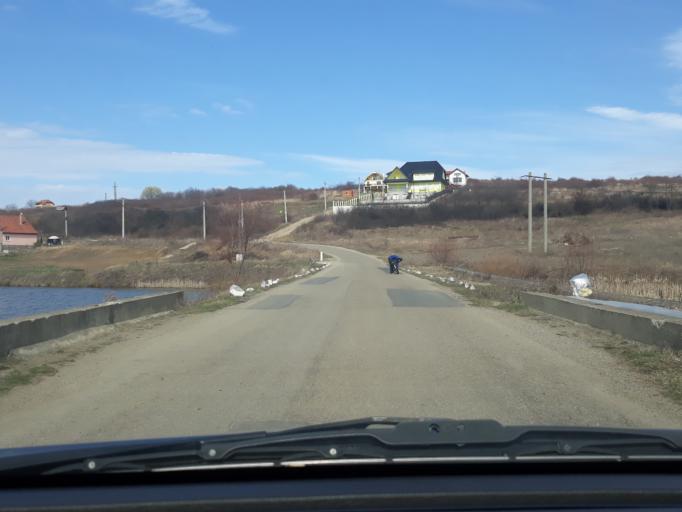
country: RO
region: Bihor
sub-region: Comuna Paleu
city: Paleu
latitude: 47.1081
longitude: 21.9638
